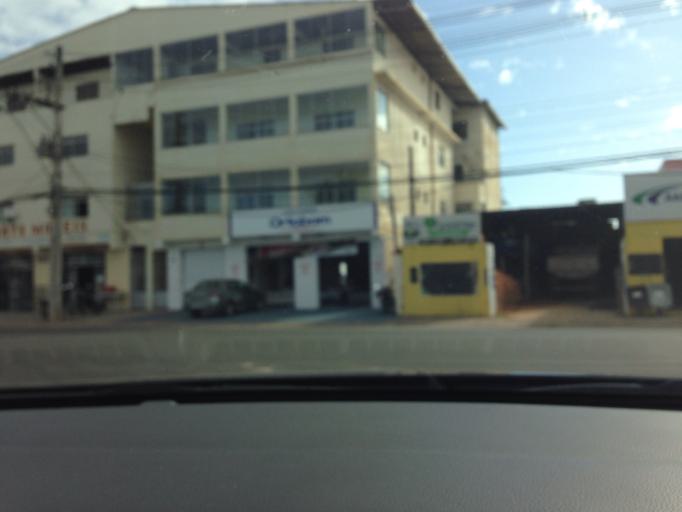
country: BR
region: Espirito Santo
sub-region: Guarapari
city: Guarapari
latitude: -20.6534
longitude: -40.4972
